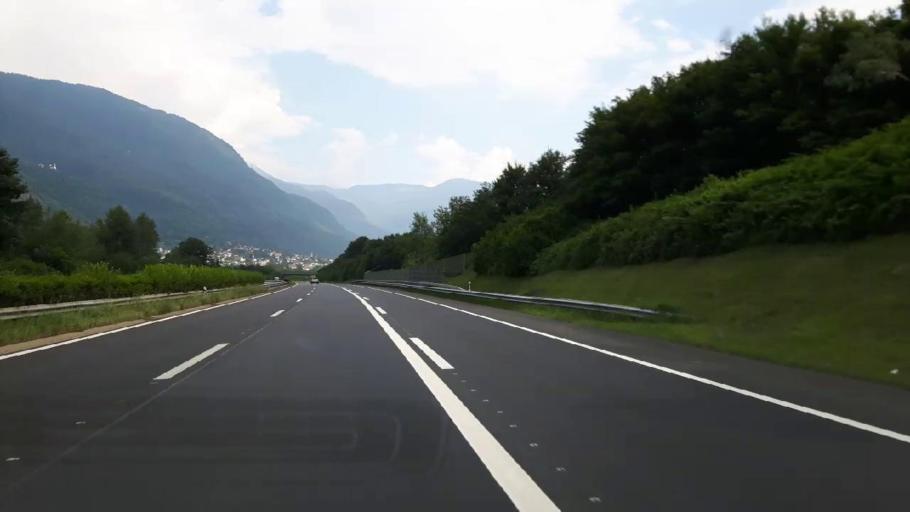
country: CH
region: Ticino
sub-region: Riviera District
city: Claro
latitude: 46.2714
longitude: 9.0006
